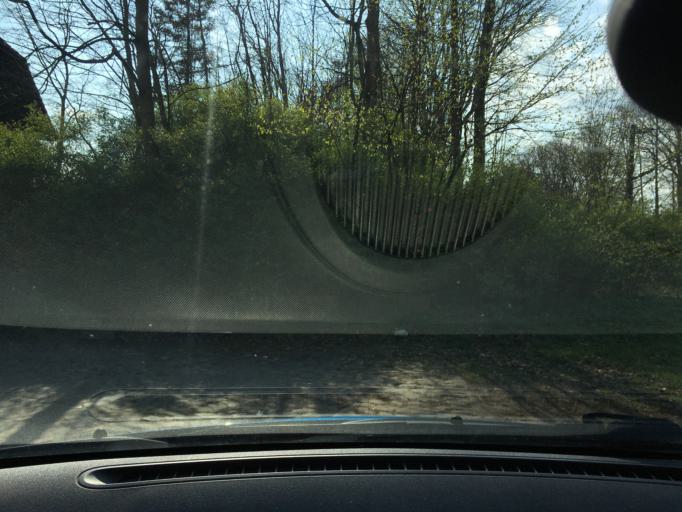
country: DE
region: Lower Saxony
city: Jesteburg
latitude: 53.3104
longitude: 9.9592
